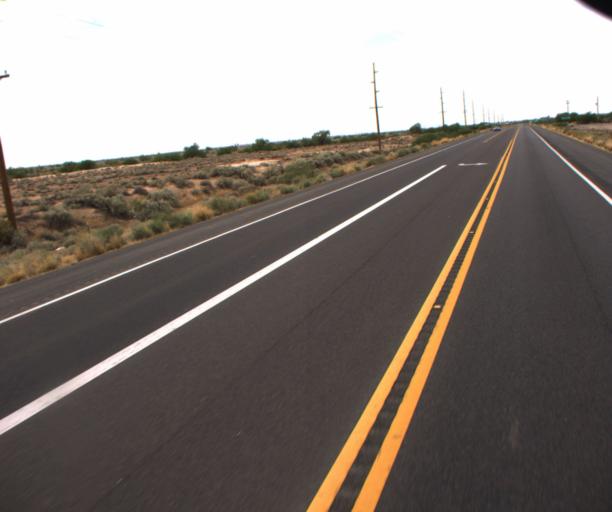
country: US
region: Arizona
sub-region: Pinal County
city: Sacaton
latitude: 33.0575
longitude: -111.6837
